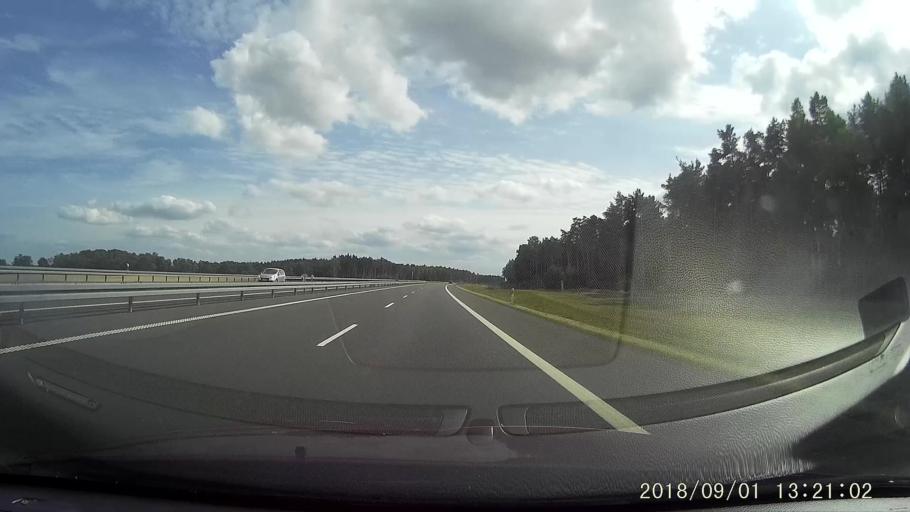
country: PL
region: West Pomeranian Voivodeship
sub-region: Powiat pyrzycki
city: Bielice
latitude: 53.1646
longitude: 14.7019
